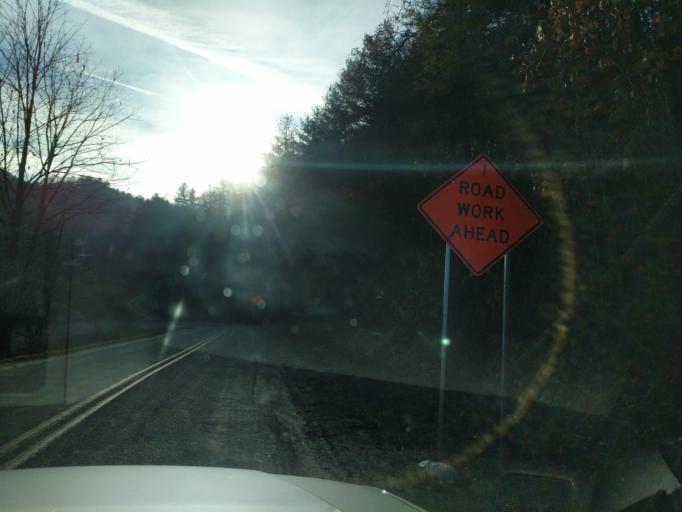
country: US
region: North Carolina
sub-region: Haywood County
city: Cove Creek
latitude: 35.6663
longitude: -83.0143
